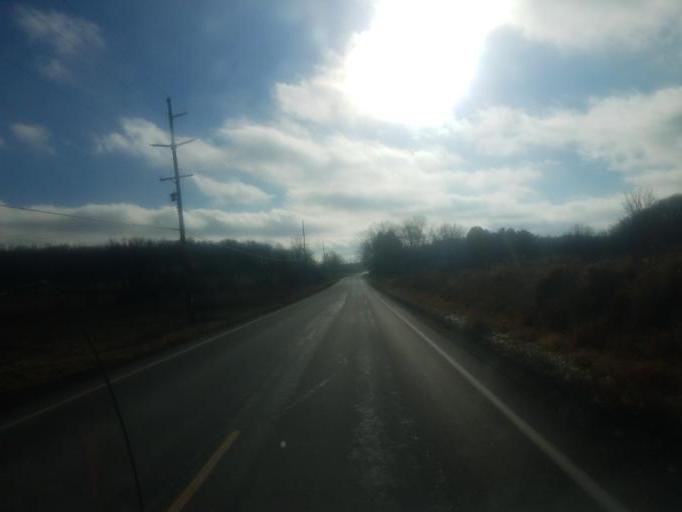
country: US
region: Ohio
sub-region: Sandusky County
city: Bellville
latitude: 40.5891
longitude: -82.5224
